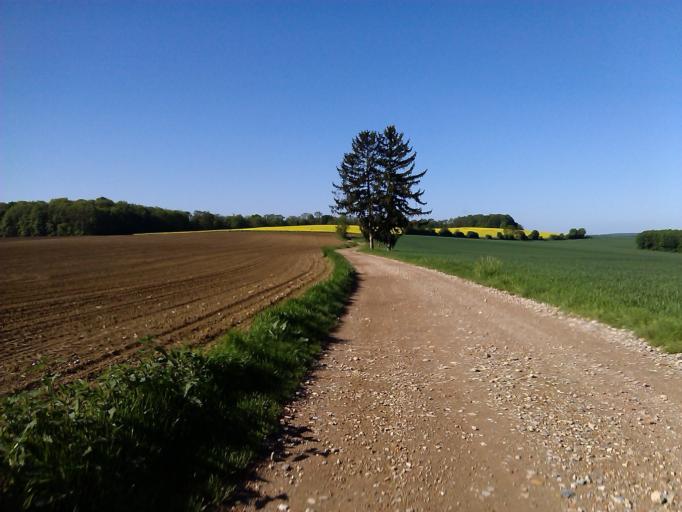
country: FR
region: Alsace
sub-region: Departement du Haut-Rhin
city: Morschwiller-le-Bas
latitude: 47.7261
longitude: 7.2593
